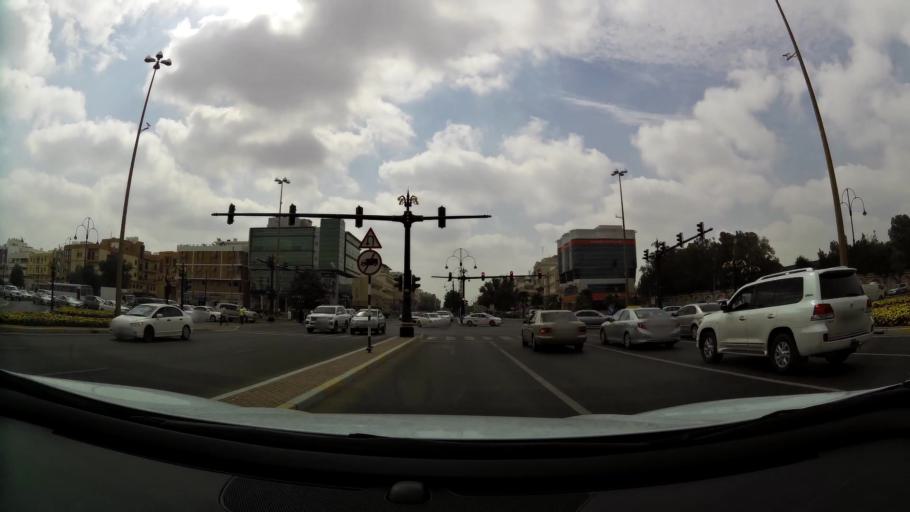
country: AE
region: Abu Dhabi
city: Al Ain
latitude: 24.2251
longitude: 55.7575
